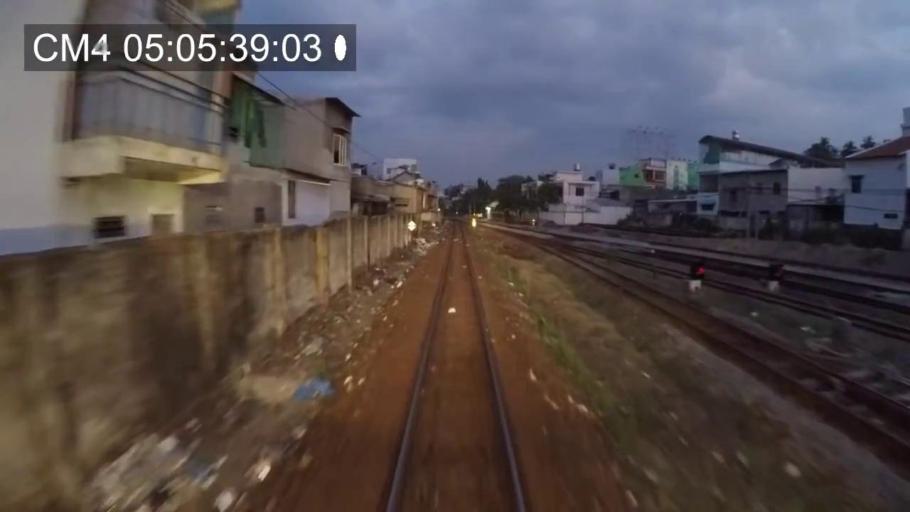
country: VN
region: Khanh Hoa
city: Nha Trang
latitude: 12.2726
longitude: 109.1763
